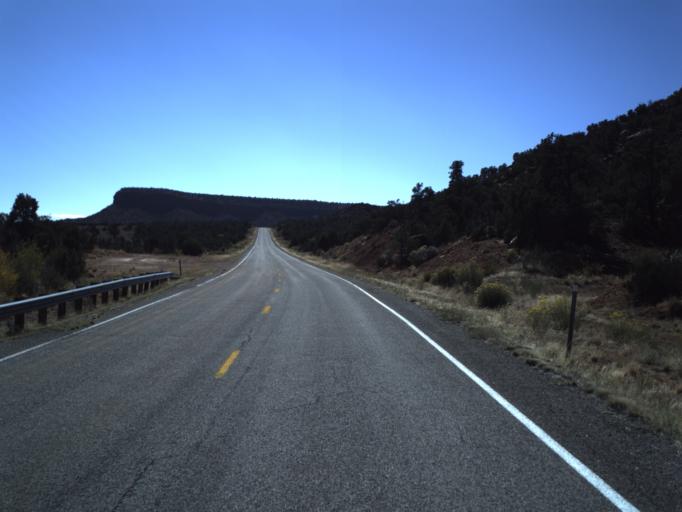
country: US
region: Utah
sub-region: San Juan County
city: Blanding
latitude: 37.5833
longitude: -110.0398
